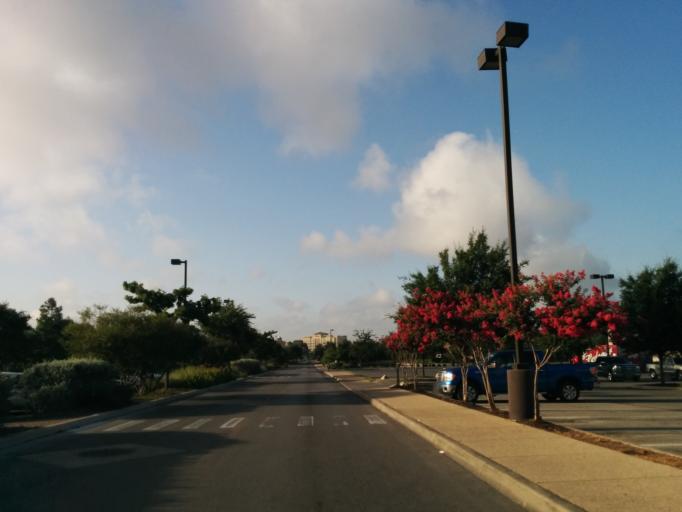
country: US
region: Texas
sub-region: Bexar County
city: Shavano Park
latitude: 29.6085
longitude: -98.6008
